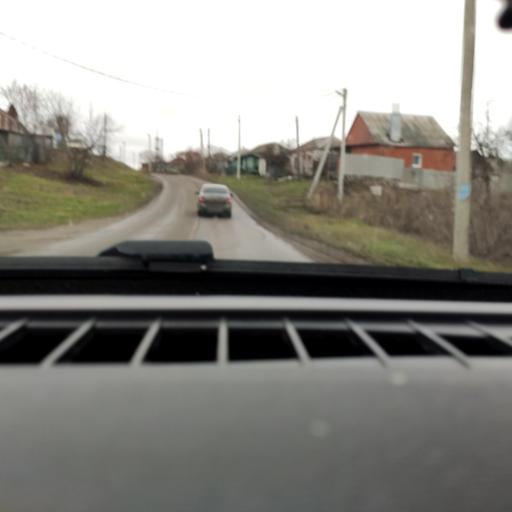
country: RU
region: Voronezj
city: Devitsa
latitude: 51.6412
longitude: 38.9404
